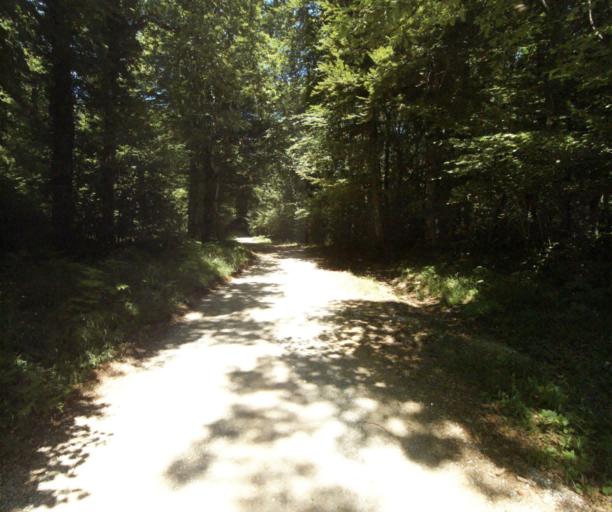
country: FR
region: Midi-Pyrenees
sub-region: Departement du Tarn
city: Dourgne
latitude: 43.4226
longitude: 2.1538
